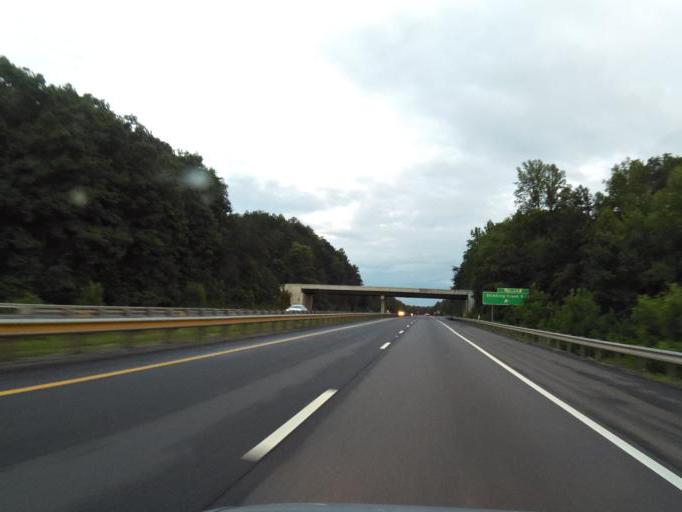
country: US
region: Tennessee
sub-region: Campbell County
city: Jacksboro
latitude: 36.4175
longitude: -84.2834
